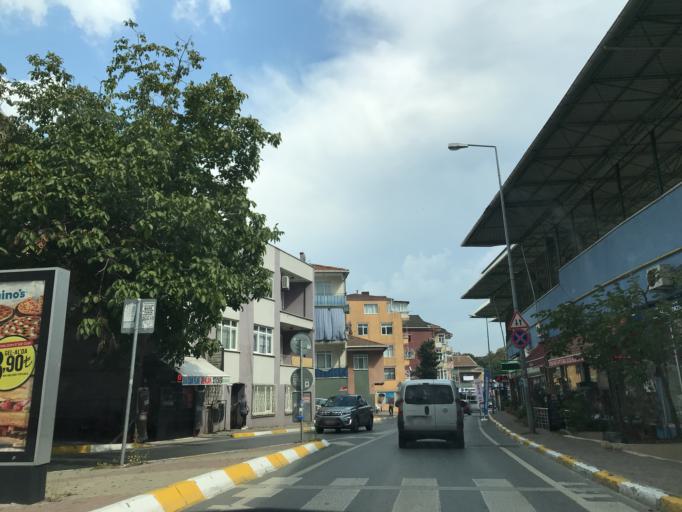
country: TR
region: Istanbul
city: Arikoey
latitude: 41.1734
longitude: 29.0499
